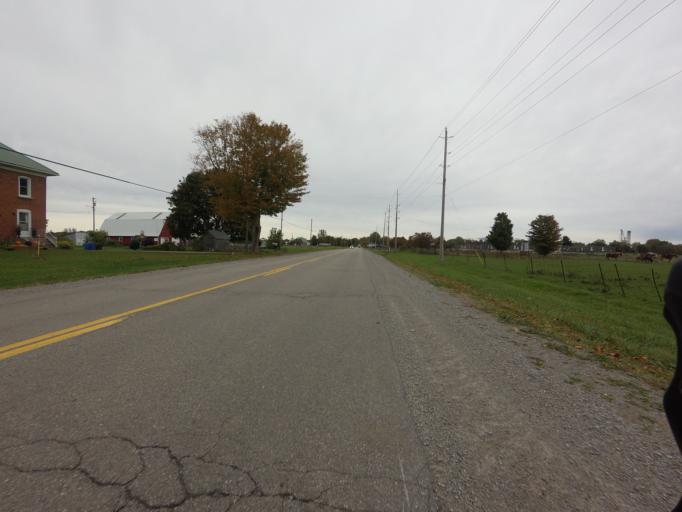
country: CA
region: Ontario
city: Brockville
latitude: 44.6580
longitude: -75.8875
